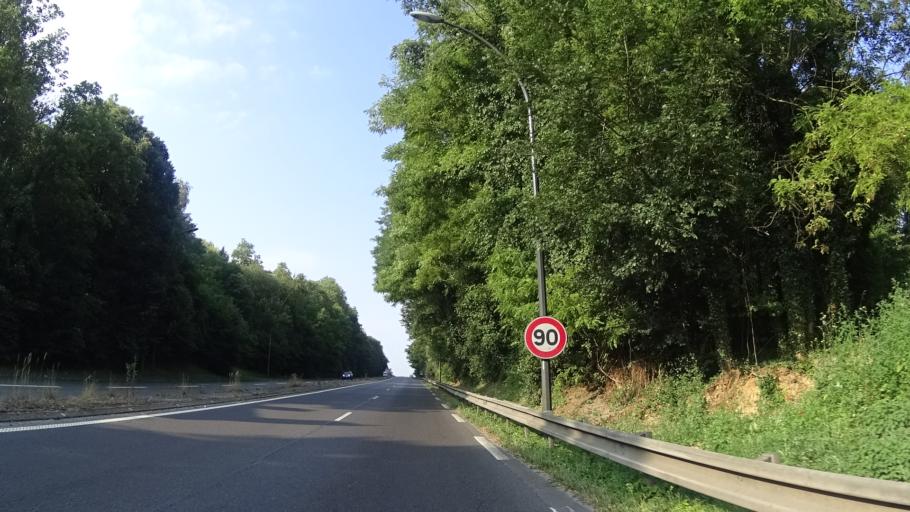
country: FR
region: Ile-de-France
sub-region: Departement du Val-d'Oise
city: Luzarches
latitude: 49.1018
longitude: 2.4223
